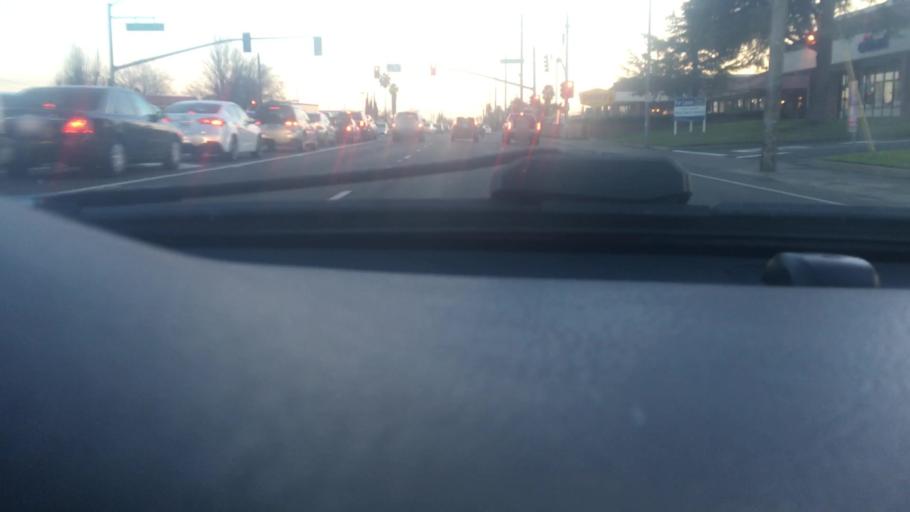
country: US
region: California
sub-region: Sacramento County
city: Carmichael
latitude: 38.6375
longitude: -121.3282
